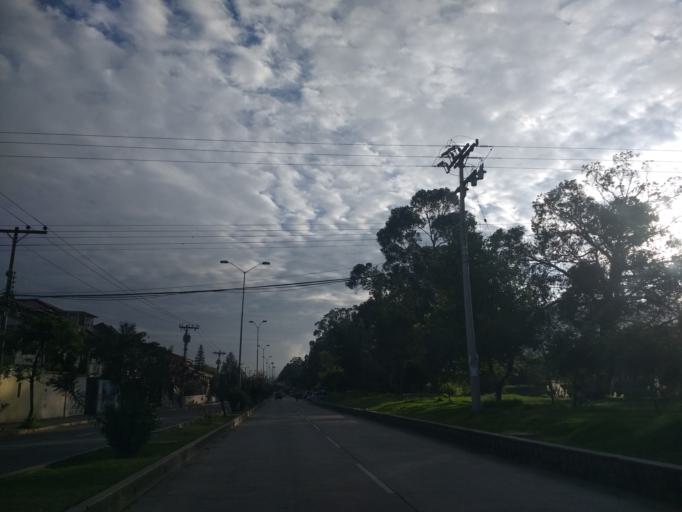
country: EC
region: Azuay
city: Cuenca
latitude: -2.9142
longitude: -78.9929
